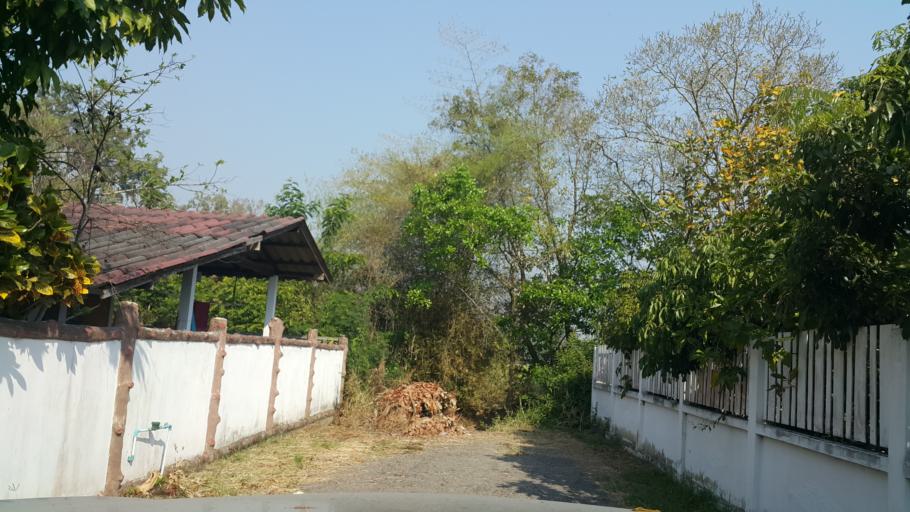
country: TH
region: Chiang Mai
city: San Kamphaeng
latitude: 18.7816
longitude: 99.0964
